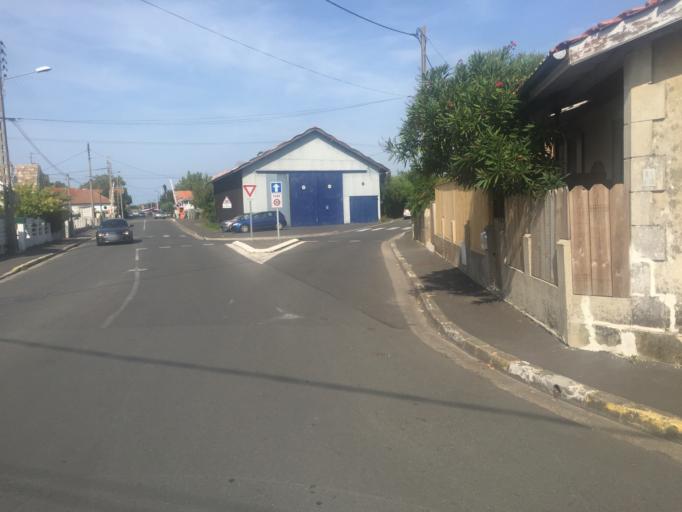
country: FR
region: Aquitaine
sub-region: Departement de la Gironde
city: La Teste-de-Buch
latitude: 44.6375
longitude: -1.1487
